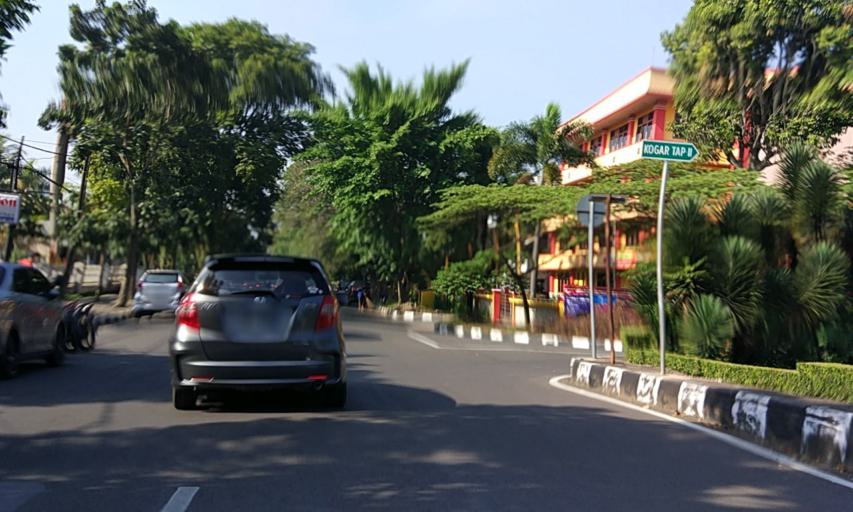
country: ID
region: West Java
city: Bandung
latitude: -6.9131
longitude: 107.6132
